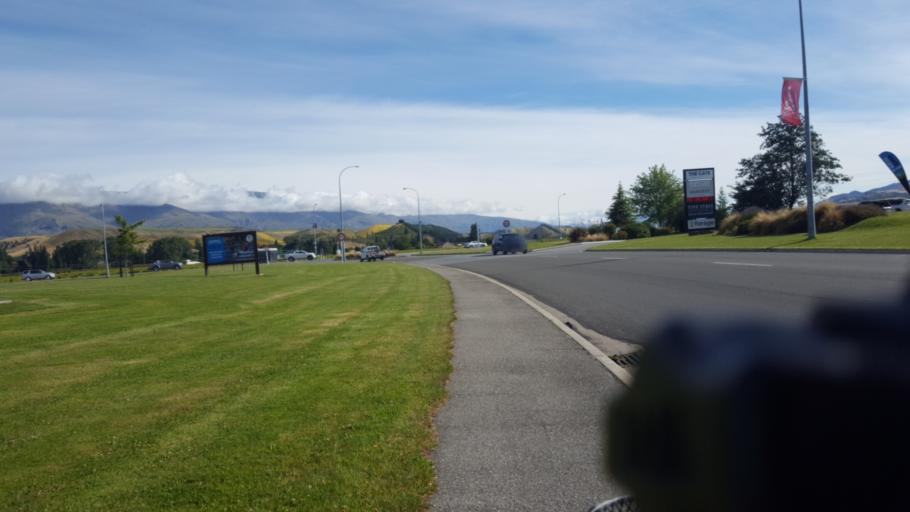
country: NZ
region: Otago
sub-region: Queenstown-Lakes District
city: Wanaka
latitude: -45.0360
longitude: 169.1995
